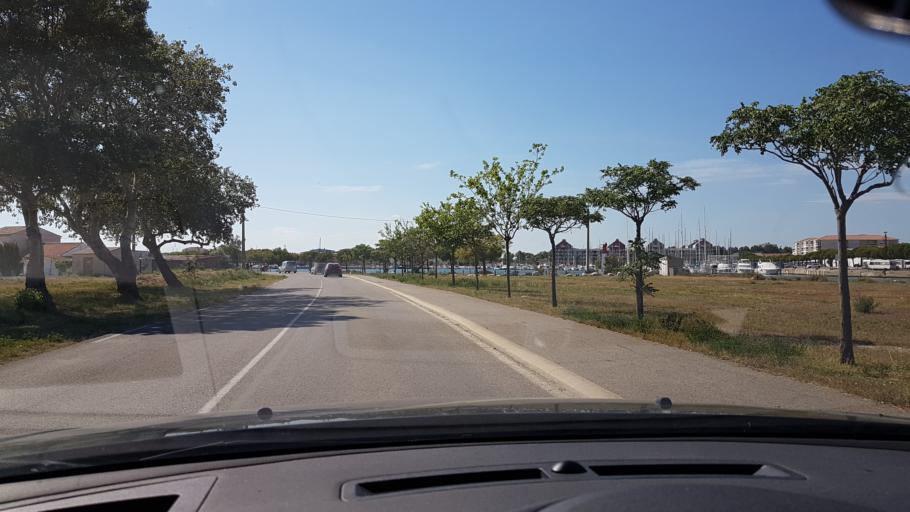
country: FR
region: Provence-Alpes-Cote d'Azur
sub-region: Departement des Bouches-du-Rhone
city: Port-Saint-Louis-du-Rhone
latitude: 43.3840
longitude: 4.8127
